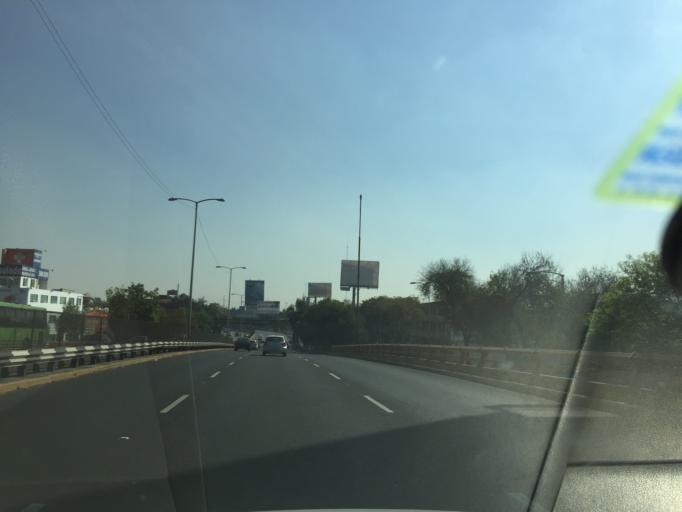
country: MX
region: Mexico City
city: Cuauhtemoc
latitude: 19.4632
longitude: -99.1532
